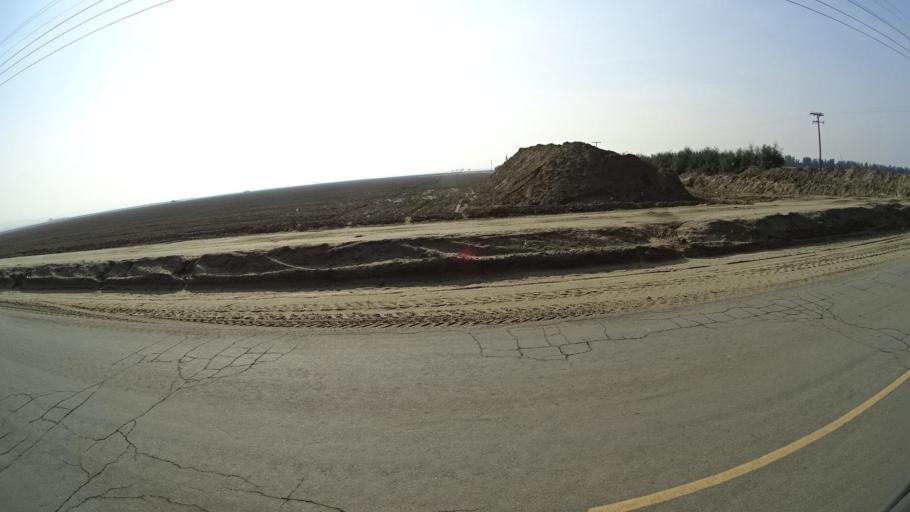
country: US
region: California
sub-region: Kern County
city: Arvin
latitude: 35.0935
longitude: -118.8633
